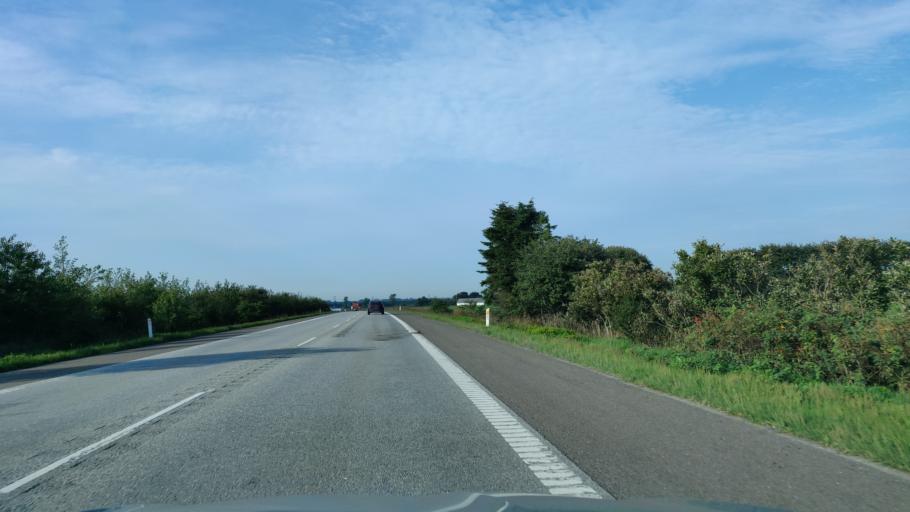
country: DK
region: North Denmark
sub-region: Vesthimmerland Kommune
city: Aars
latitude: 56.8132
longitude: 9.6624
